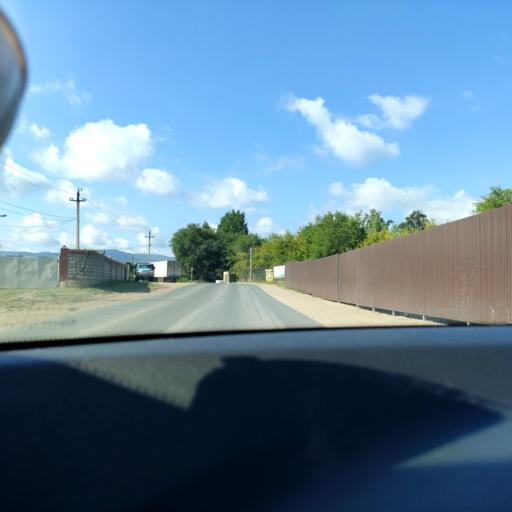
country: RU
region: Samara
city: Volzhskiy
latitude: 53.4345
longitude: 50.1038
